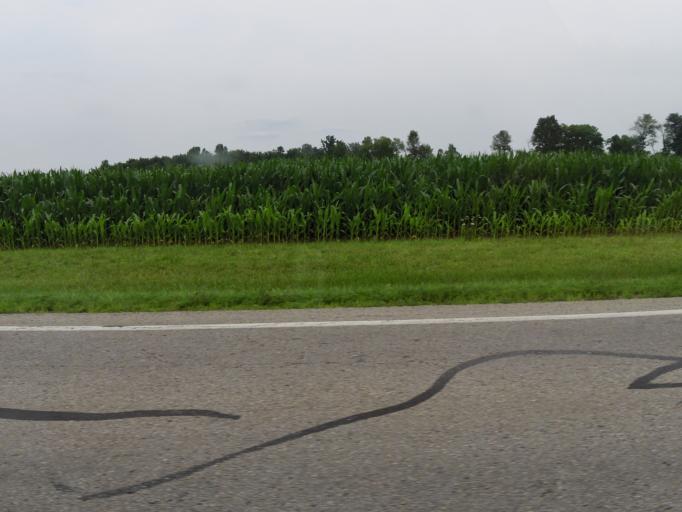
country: US
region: Ohio
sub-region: Clinton County
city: Wilmington
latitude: 39.4834
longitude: -83.9269
